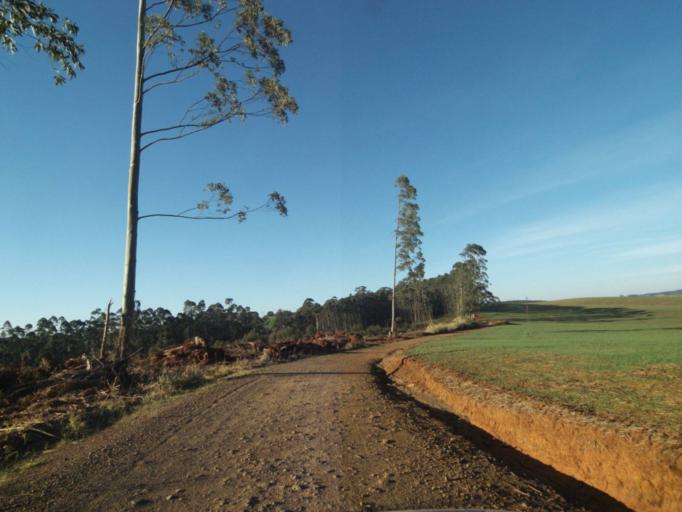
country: BR
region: Parana
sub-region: Telemaco Borba
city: Telemaco Borba
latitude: -24.4809
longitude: -50.5929
